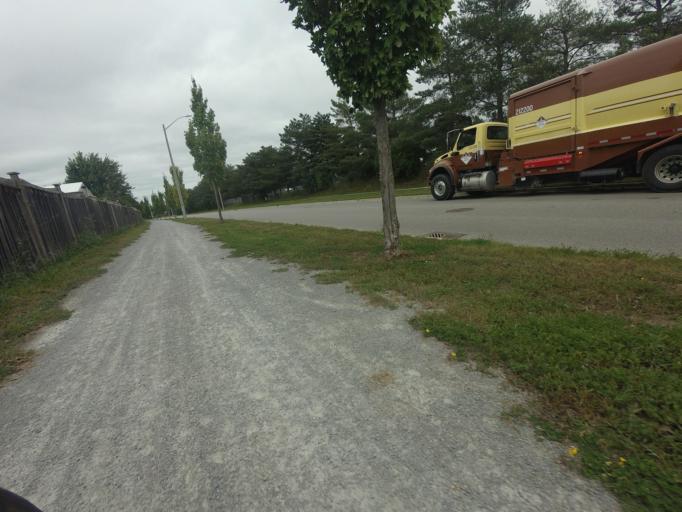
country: CA
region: Ontario
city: Omemee
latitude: 44.3386
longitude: -78.7477
